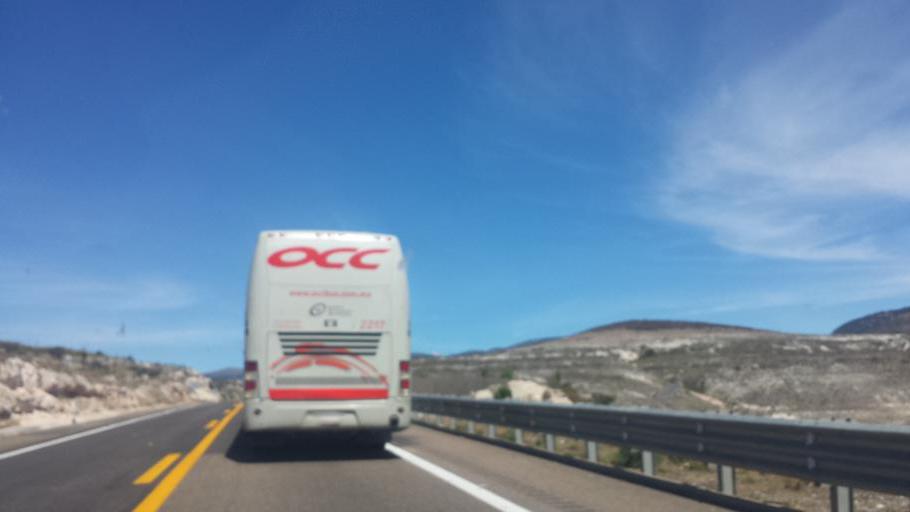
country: MX
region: Oaxaca
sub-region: Villa Tejupam de la Union
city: Villa Tejupam de la Union
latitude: 17.9036
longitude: -97.3664
